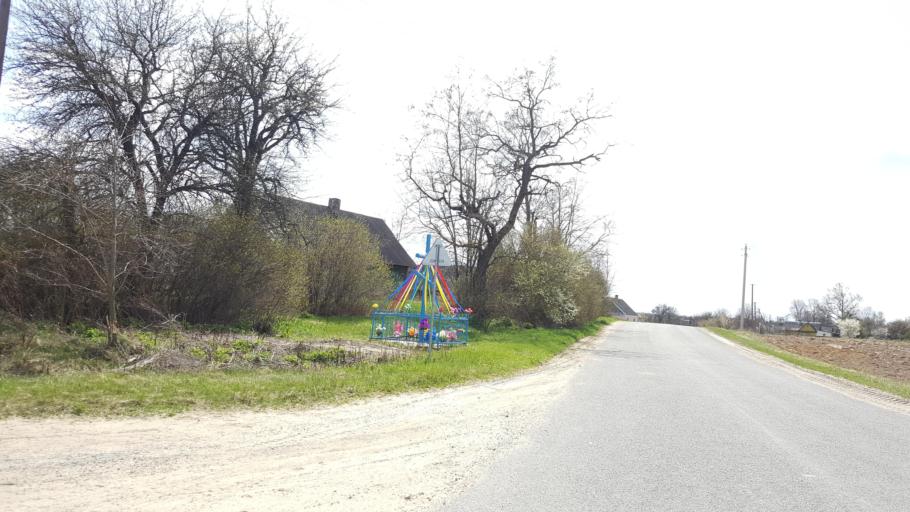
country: BY
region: Brest
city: Kamyanyets
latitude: 52.3852
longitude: 23.7467
